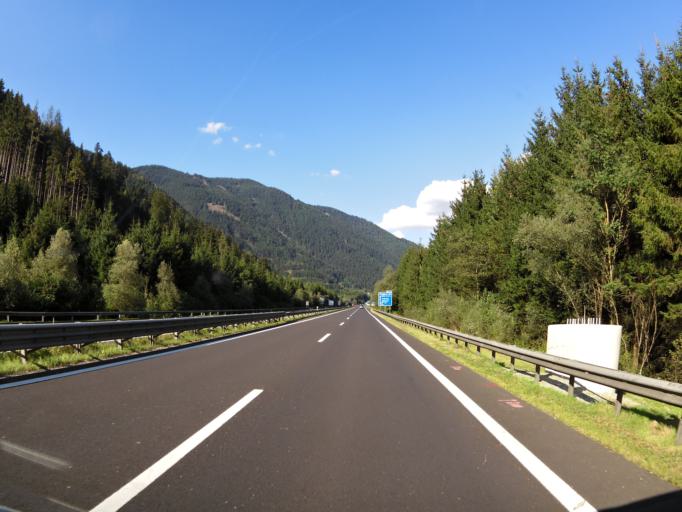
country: AT
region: Styria
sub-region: Politischer Bezirk Liezen
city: Selzthal
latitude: 47.5661
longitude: 14.3084
